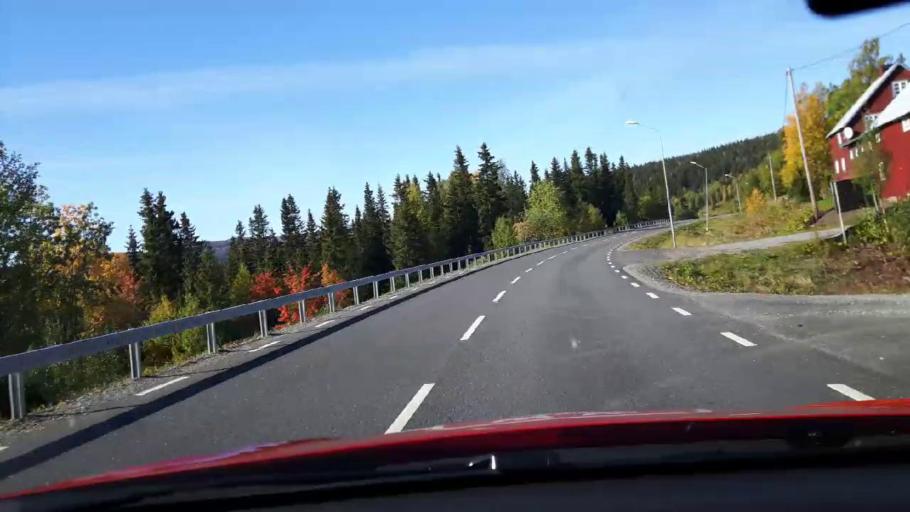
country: NO
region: Nord-Trondelag
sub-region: Royrvik
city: Royrvik
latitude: 64.8315
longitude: 14.1140
